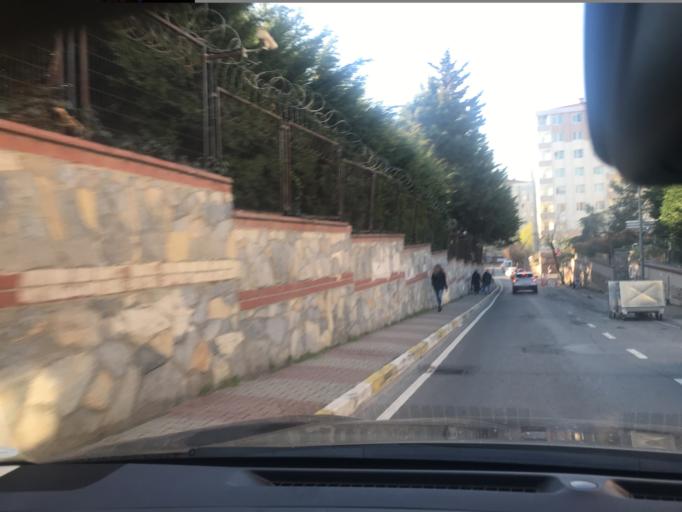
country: TR
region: Istanbul
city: Umraniye
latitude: 41.0314
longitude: 29.1750
